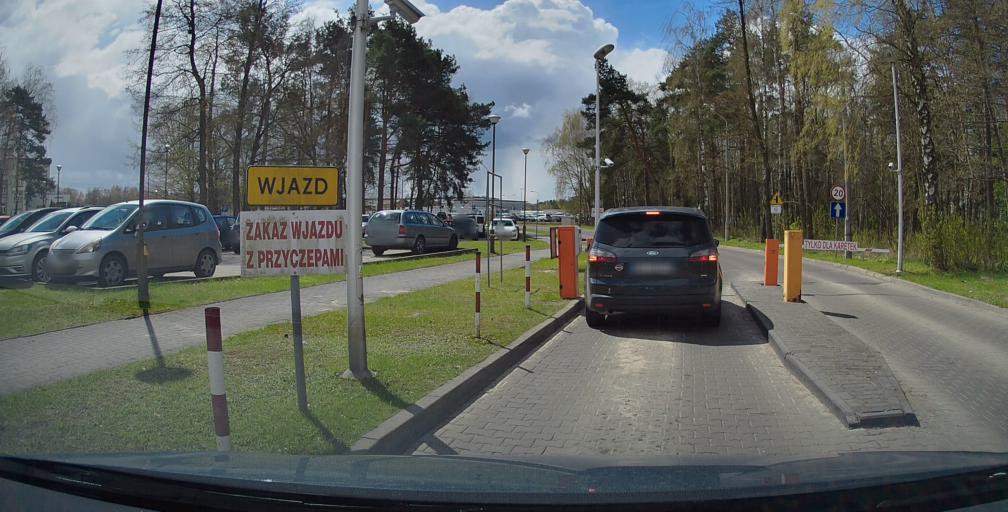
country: PL
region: Masovian Voivodeship
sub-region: Ostroleka
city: Ostroleka
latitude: 53.0638
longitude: 21.5881
